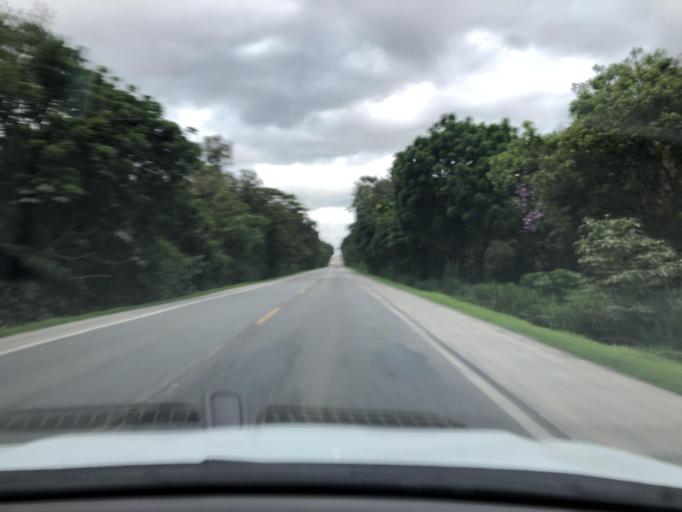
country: BR
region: Santa Catarina
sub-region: Sao Francisco Do Sul
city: Sao Francisco do Sul
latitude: -26.3178
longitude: -48.6463
